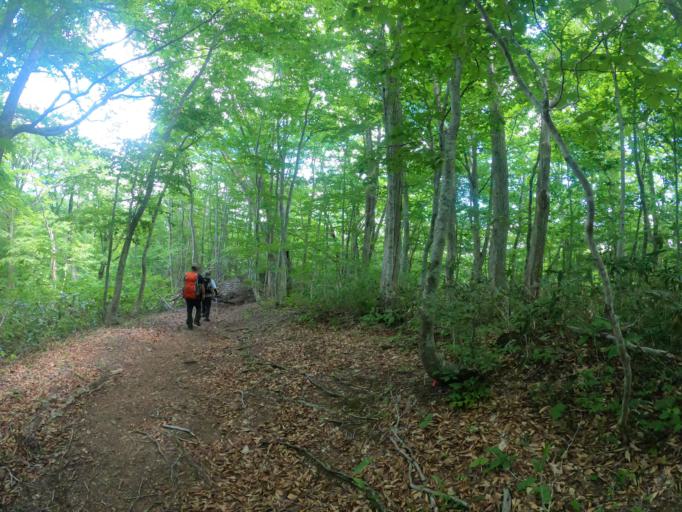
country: JP
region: Iwate
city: Ichinoseki
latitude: 38.9223
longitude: 140.7983
